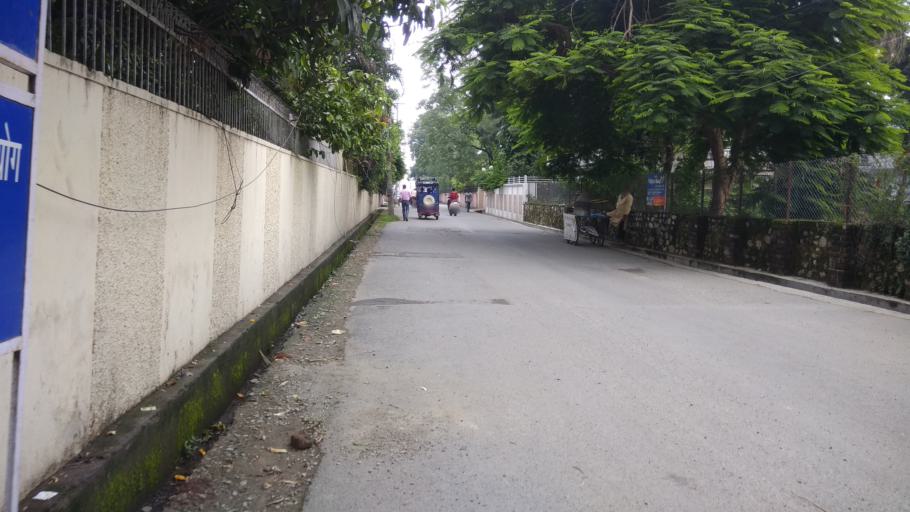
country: IN
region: Uttarakhand
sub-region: Dehradun
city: Dehradun
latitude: 30.3141
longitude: 78.0592
